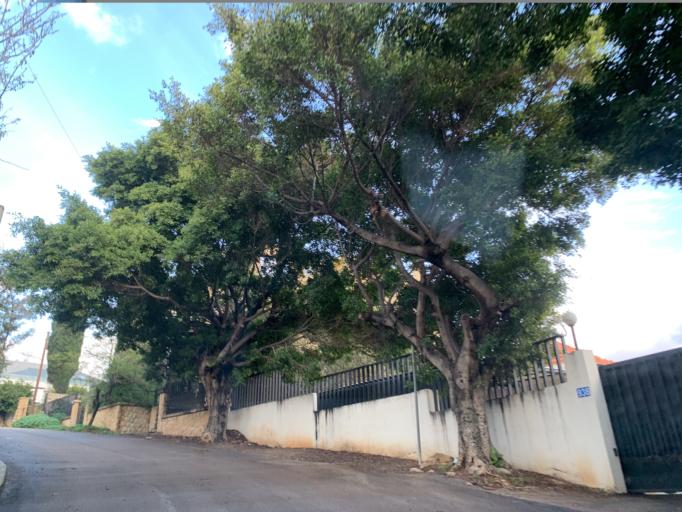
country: LB
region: Mont-Liban
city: Baabda
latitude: 33.8508
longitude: 35.5786
